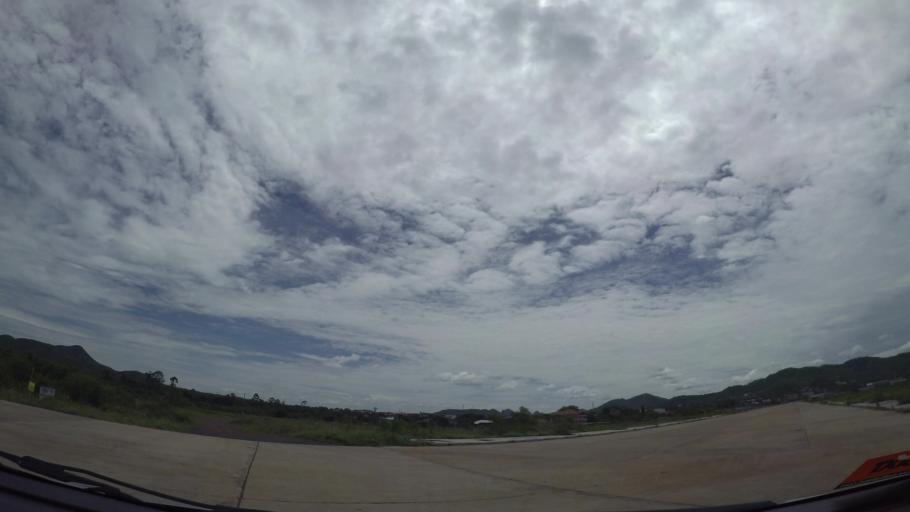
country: TH
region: Chon Buri
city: Sattahip
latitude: 12.6976
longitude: 100.8832
